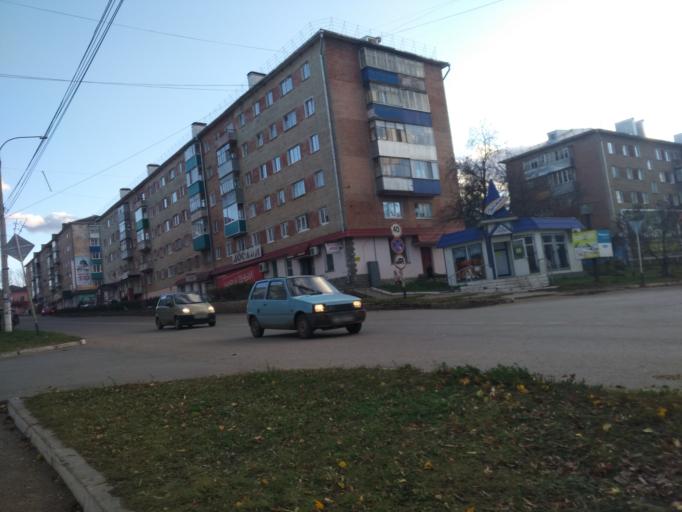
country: RU
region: Kirov
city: Vyatskiye Polyany
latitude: 56.2276
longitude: 51.0723
